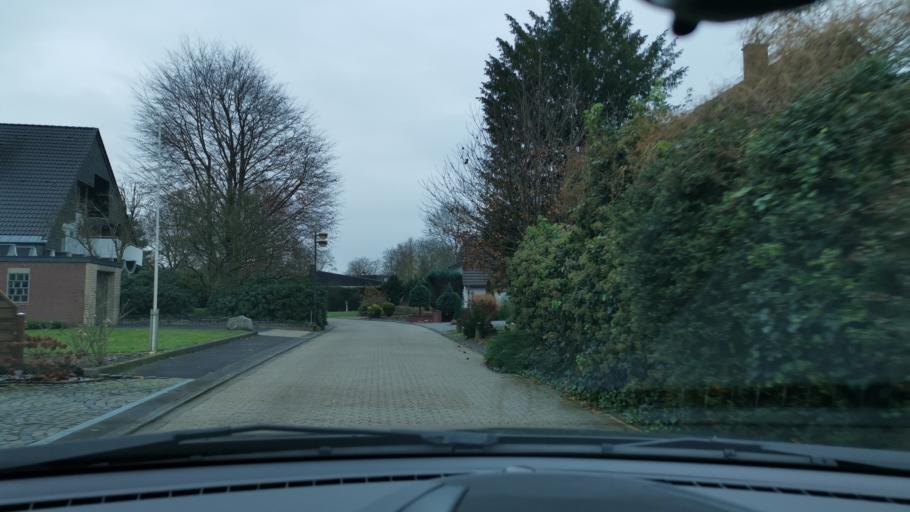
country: DE
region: North Rhine-Westphalia
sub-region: Regierungsbezirk Dusseldorf
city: Neubrueck
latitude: 51.1302
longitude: 6.6453
